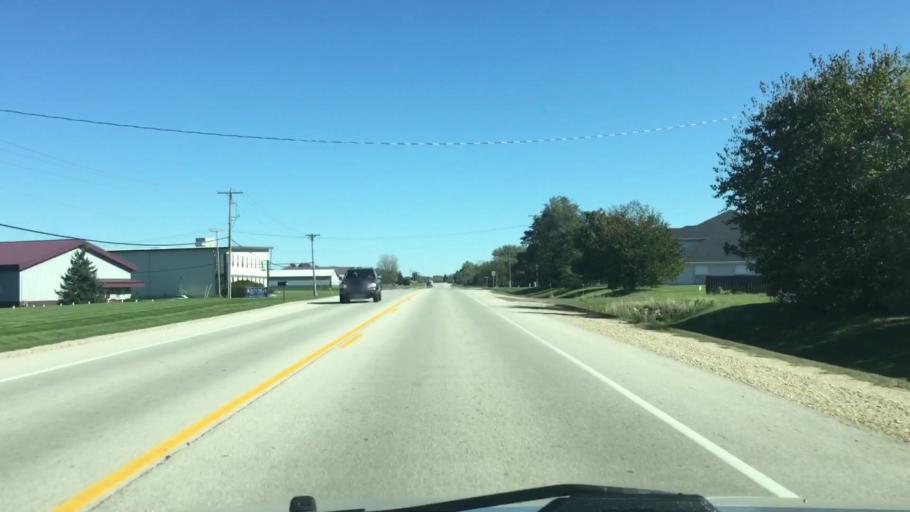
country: US
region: Wisconsin
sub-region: Waukesha County
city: North Prairie
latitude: 42.9362
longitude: -88.3948
